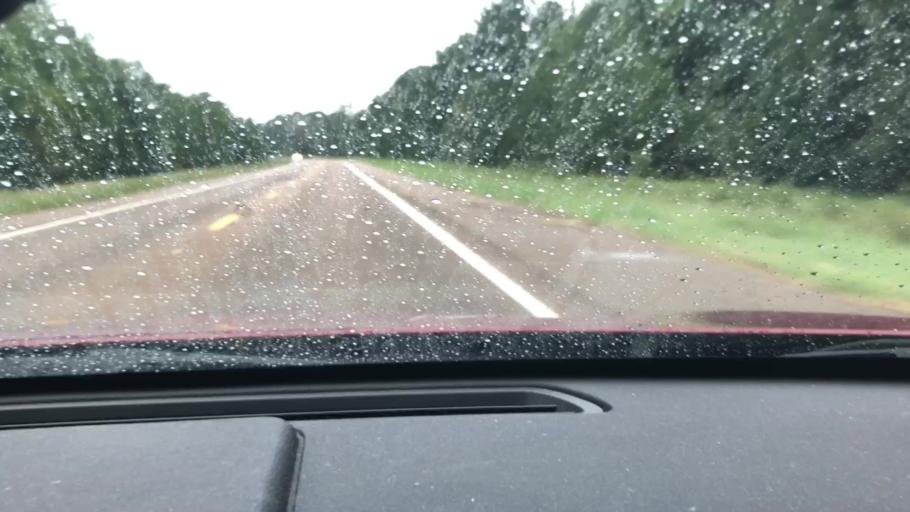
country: US
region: Arkansas
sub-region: Columbia County
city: Magnolia
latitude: 33.3005
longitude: -93.2664
